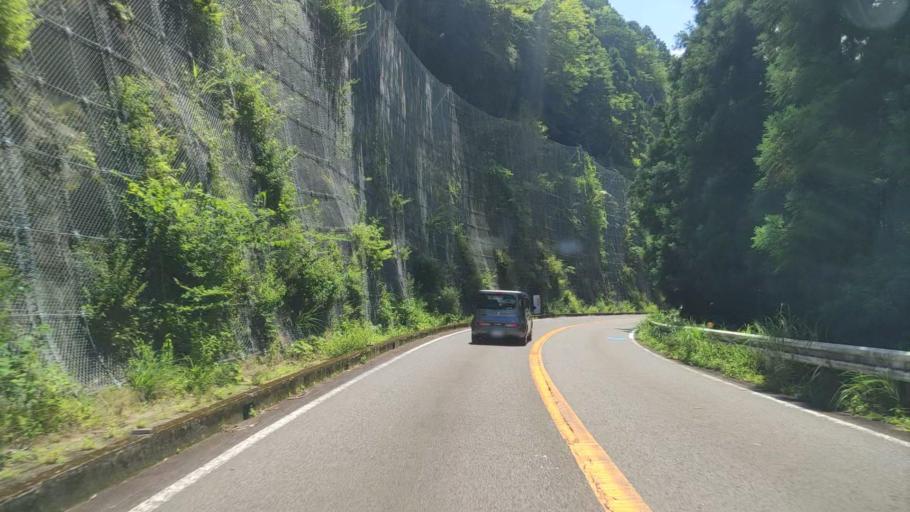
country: JP
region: Mie
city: Owase
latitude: 33.9814
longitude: 136.1067
